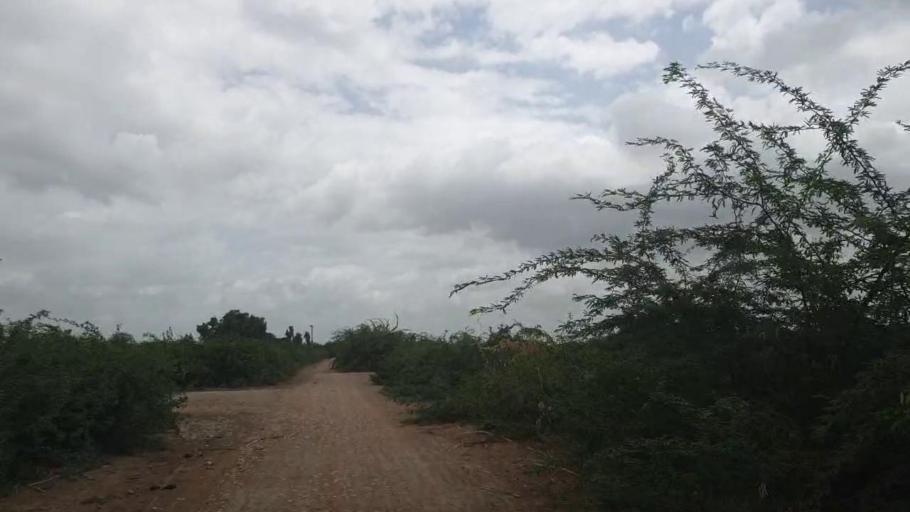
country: PK
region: Sindh
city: Badin
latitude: 24.6378
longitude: 68.9488
